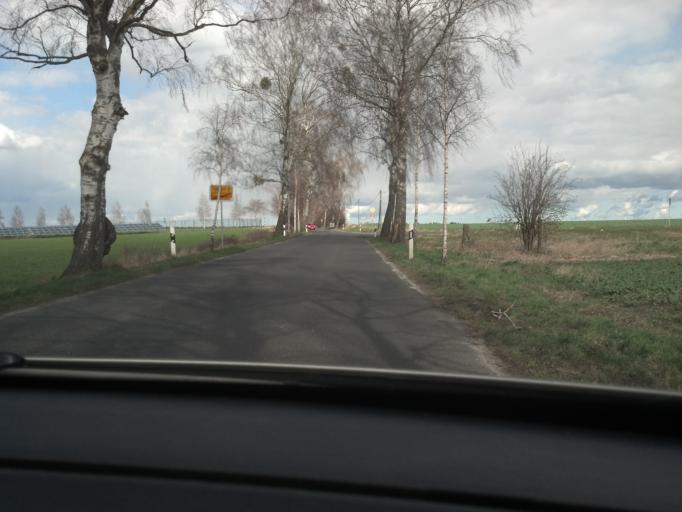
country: DE
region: Mecklenburg-Vorpommern
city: Burg Stargard
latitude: 53.5036
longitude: 13.3235
